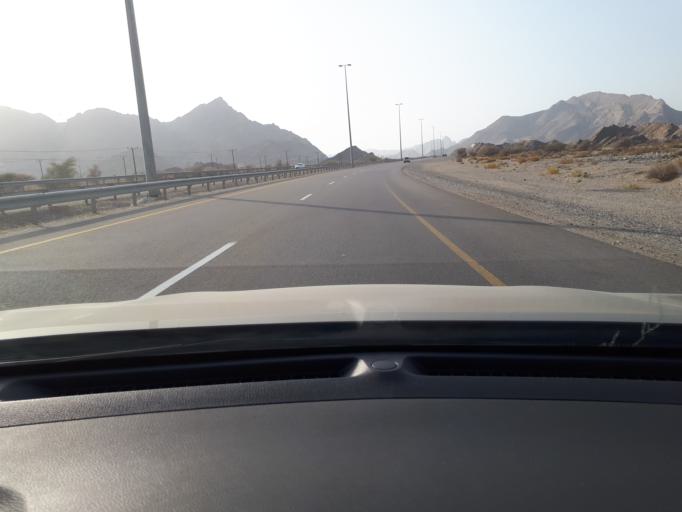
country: OM
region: Muhafazat Masqat
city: Muscat
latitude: 23.3347
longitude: 58.7038
